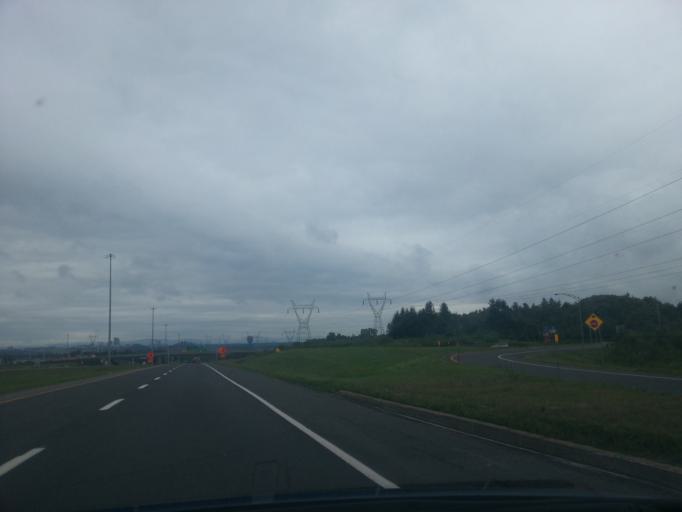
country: CA
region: Quebec
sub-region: Chaudiere-Appalaches
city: Breakeyville
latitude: 46.7090
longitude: -71.2965
